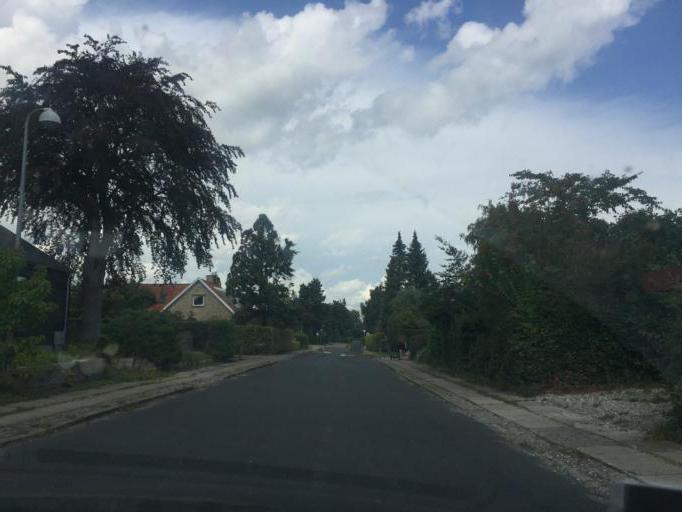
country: DK
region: Capital Region
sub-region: Rudersdal Kommune
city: Holte
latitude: 55.7904
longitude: 12.4523
